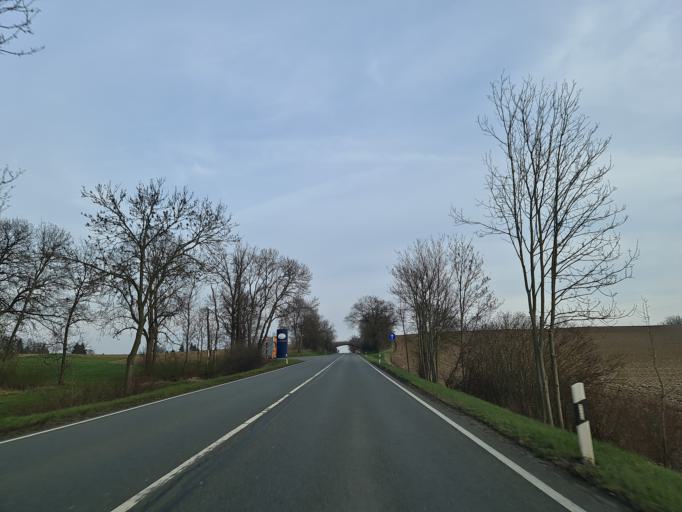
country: DE
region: Saxony
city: Plauen
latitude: 50.4640
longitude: 12.1532
